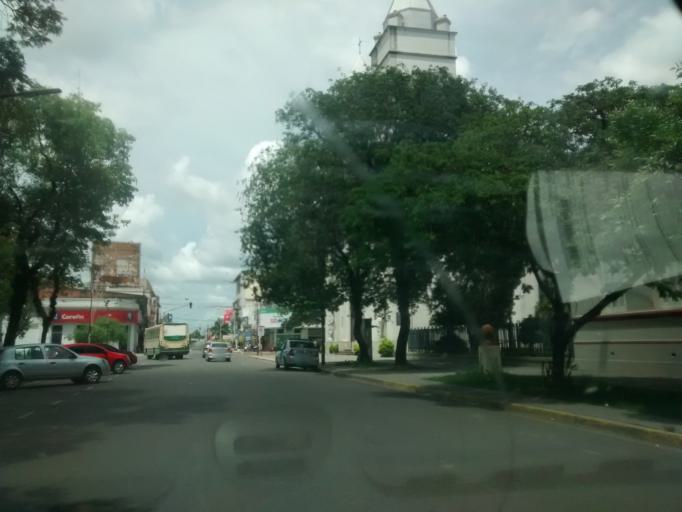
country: AR
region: Chaco
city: Resistencia
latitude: -27.4506
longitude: -58.9876
